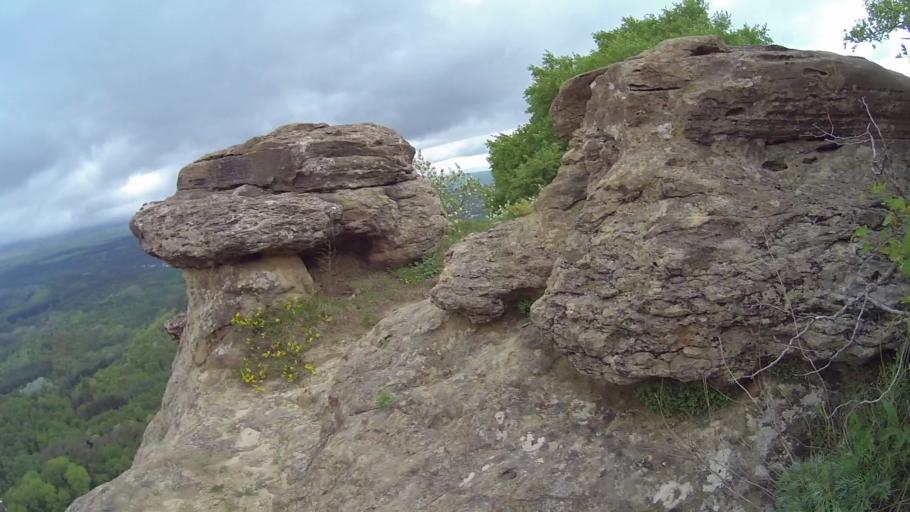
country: RU
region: Stavropol'skiy
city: Kislovodsk
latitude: 43.8870
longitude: 42.7613
